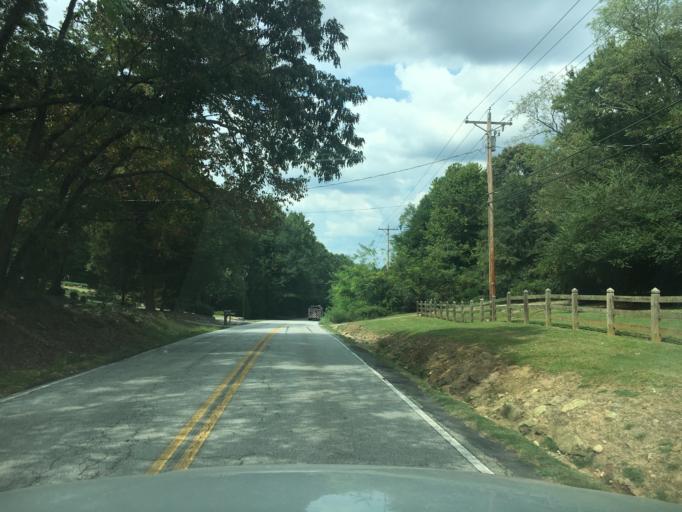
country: US
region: South Carolina
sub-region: Greenville County
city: Five Forks
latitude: 34.8364
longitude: -82.2275
